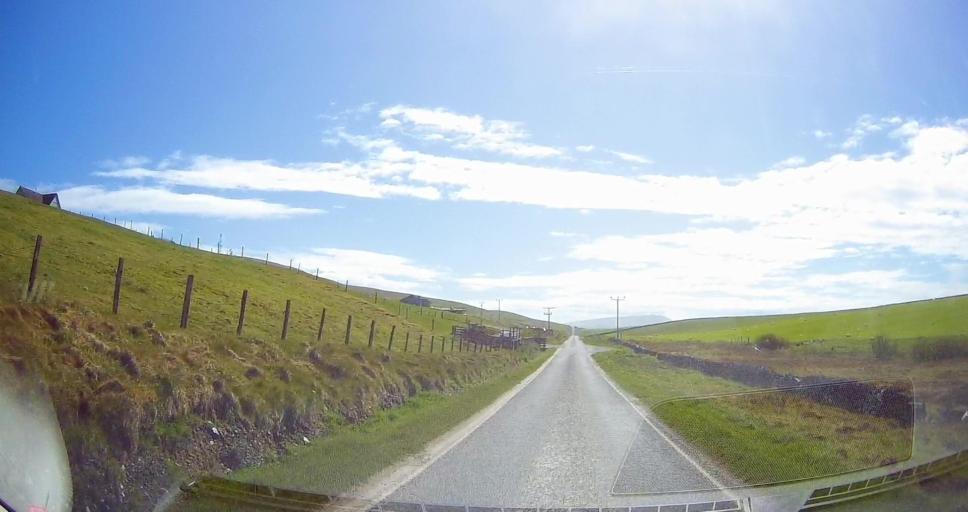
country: GB
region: Scotland
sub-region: Shetland Islands
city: Sandwick
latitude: 59.9715
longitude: -1.3164
